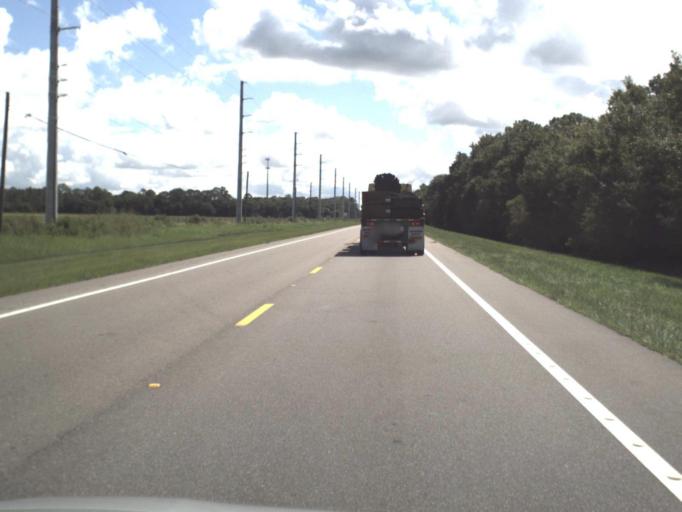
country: US
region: Florida
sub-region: Sarasota County
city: The Meadows
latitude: 27.4284
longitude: -82.3789
